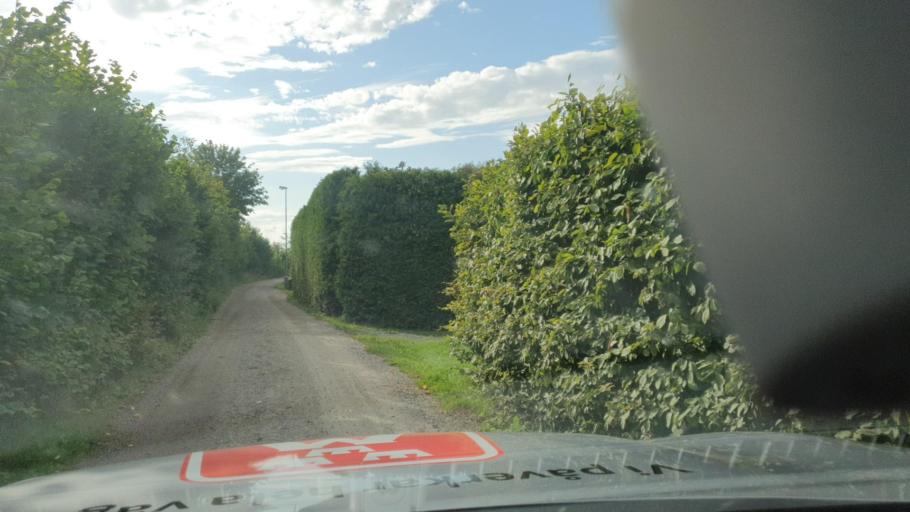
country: SE
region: Skane
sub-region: Bromolla Kommun
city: Bromoella
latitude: 56.0932
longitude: 14.4976
